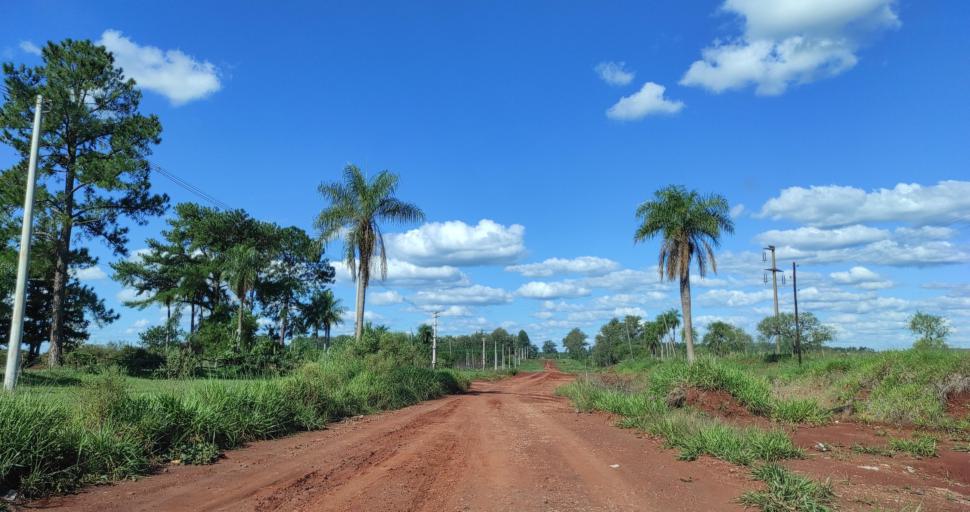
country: AR
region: Misiones
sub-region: Departamento de Candelaria
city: Candelaria
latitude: -27.4640
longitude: -55.7204
